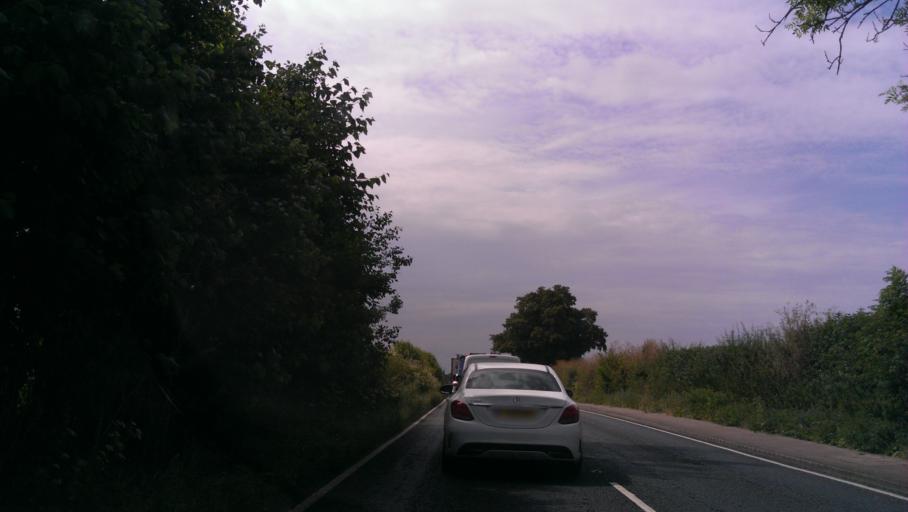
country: GB
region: England
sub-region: Kent
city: Teynham
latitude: 51.3222
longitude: 0.8225
